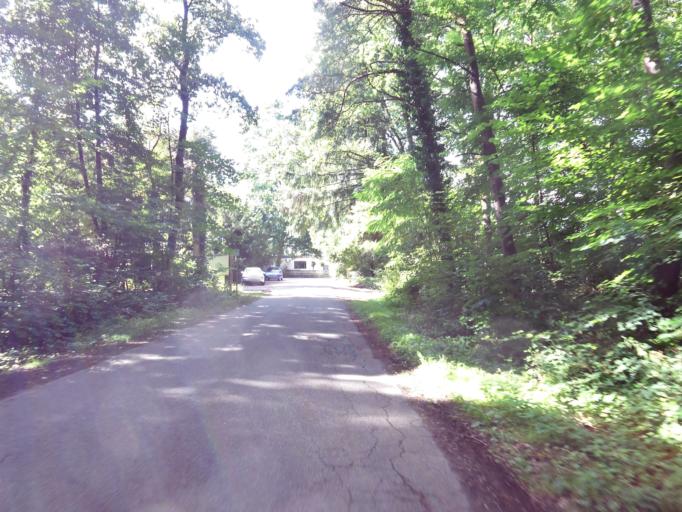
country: DE
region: Rheinland-Pfalz
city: Hanhofen
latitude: 49.3468
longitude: 8.3241
